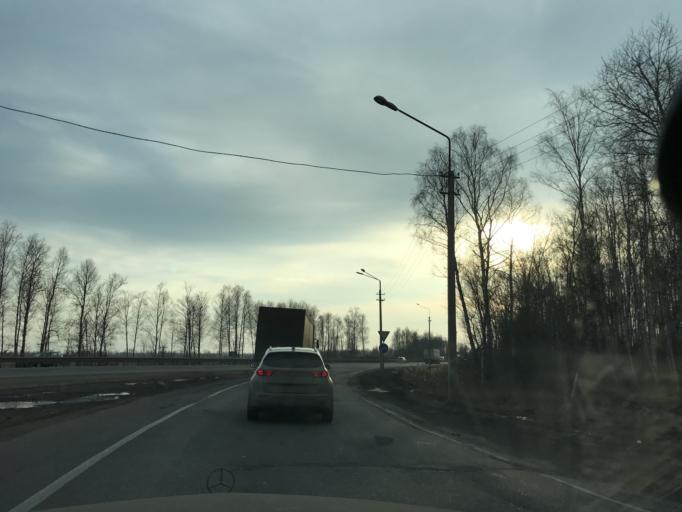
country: RU
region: Vladimir
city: Vorsha
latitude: 56.0802
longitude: 40.1944
